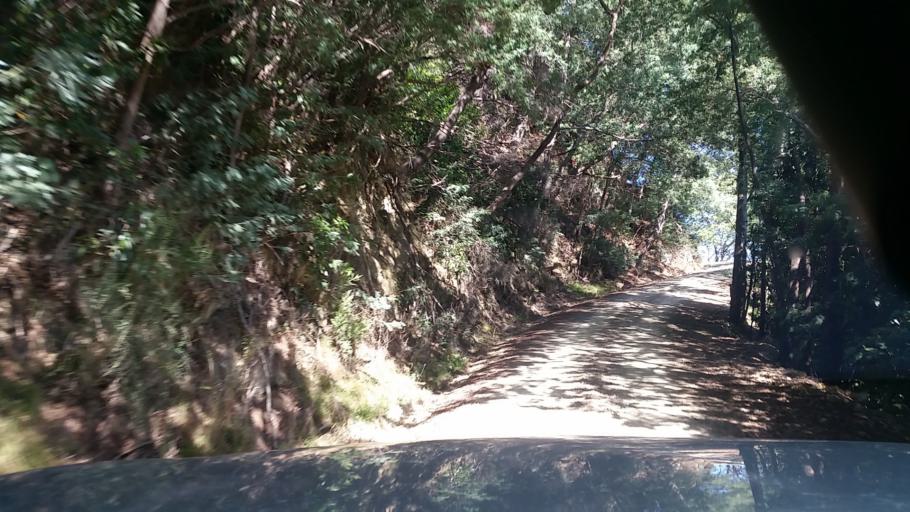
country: NZ
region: Marlborough
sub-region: Marlborough District
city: Picton
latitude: -41.3050
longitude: 174.1773
